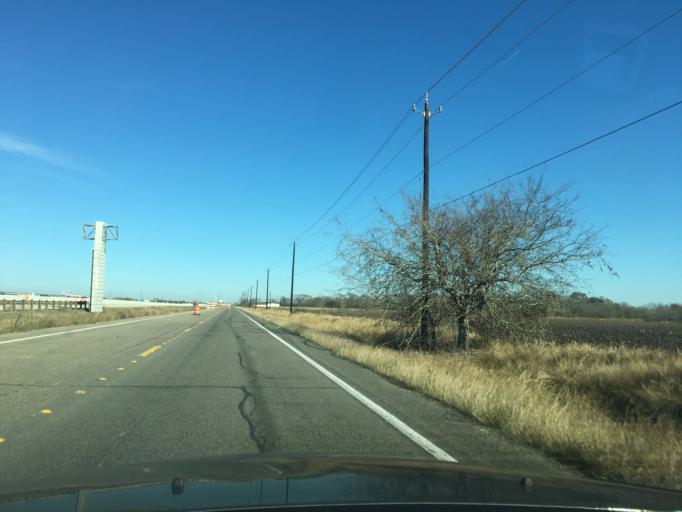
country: US
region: Texas
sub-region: Wharton County
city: East Bernard
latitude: 29.4740
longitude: -95.9550
